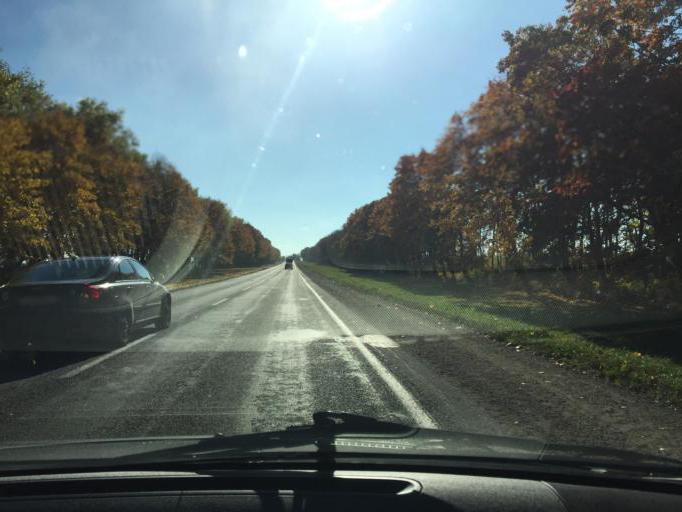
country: BY
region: Minsk
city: Salihorsk
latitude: 52.8858
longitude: 27.4703
